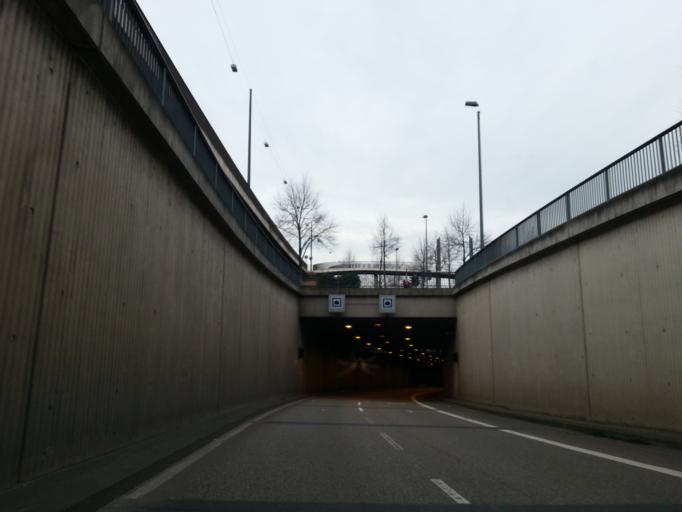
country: DE
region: North Rhine-Westphalia
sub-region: Regierungsbezirk Dusseldorf
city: Dusseldorf
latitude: 51.2182
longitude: 6.7683
